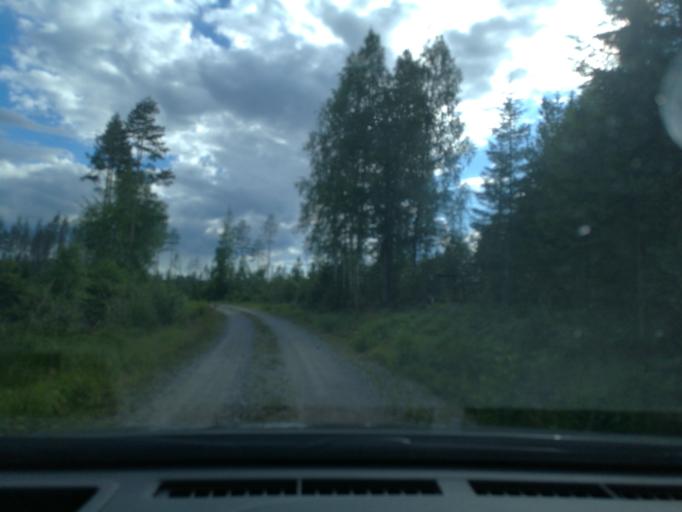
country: SE
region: Vaestmanland
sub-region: Surahammars Kommun
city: Ramnas
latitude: 59.8400
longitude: 16.2766
